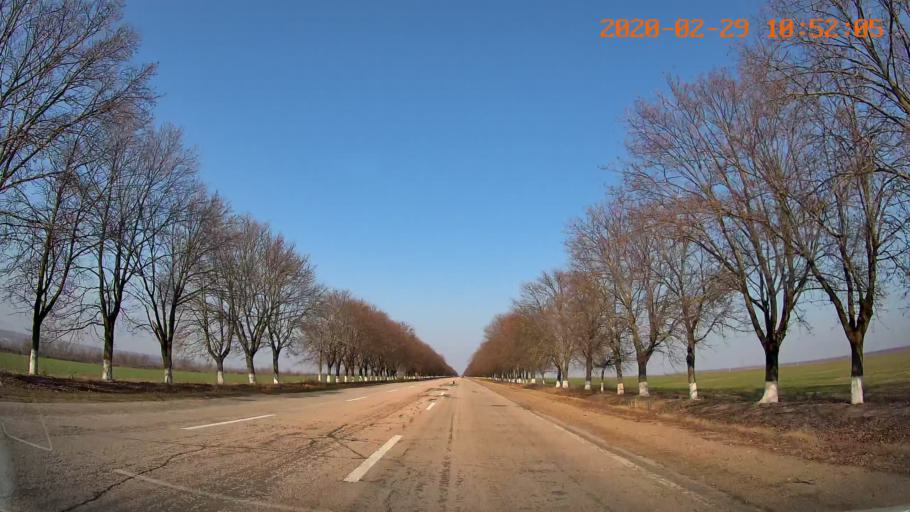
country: MD
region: Telenesti
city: Grigoriopol
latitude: 47.1008
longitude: 29.3549
